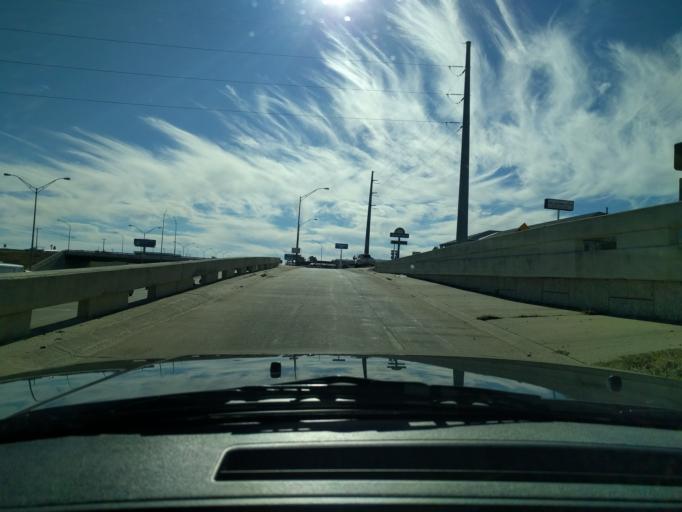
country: US
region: Oklahoma
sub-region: Cleveland County
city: Moore
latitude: 35.3858
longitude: -97.4954
